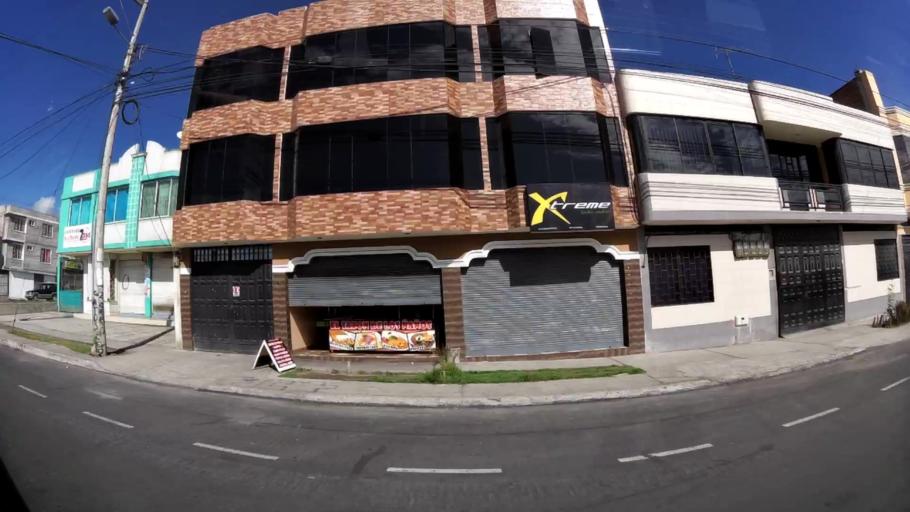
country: EC
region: Chimborazo
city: Riobamba
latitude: -1.6581
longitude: -78.6724
